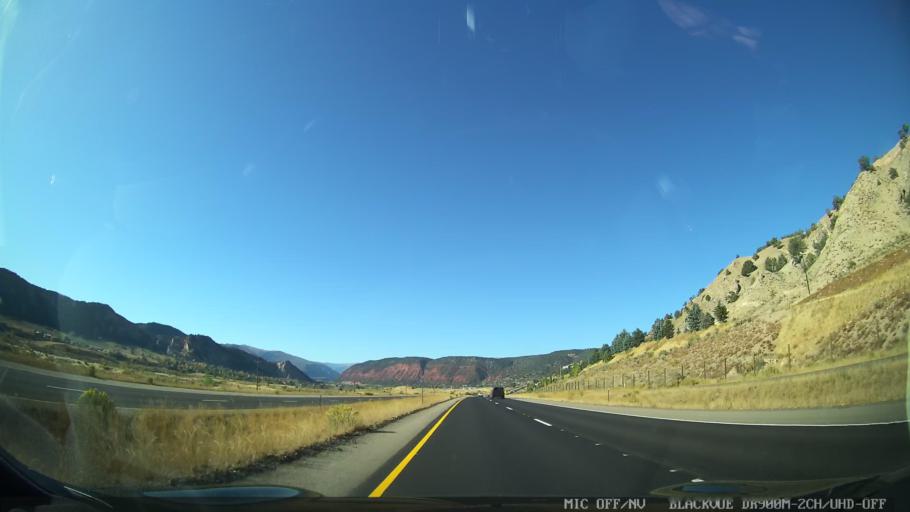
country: US
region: Colorado
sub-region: Garfield County
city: Carbondale
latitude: 39.4486
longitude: -107.2611
